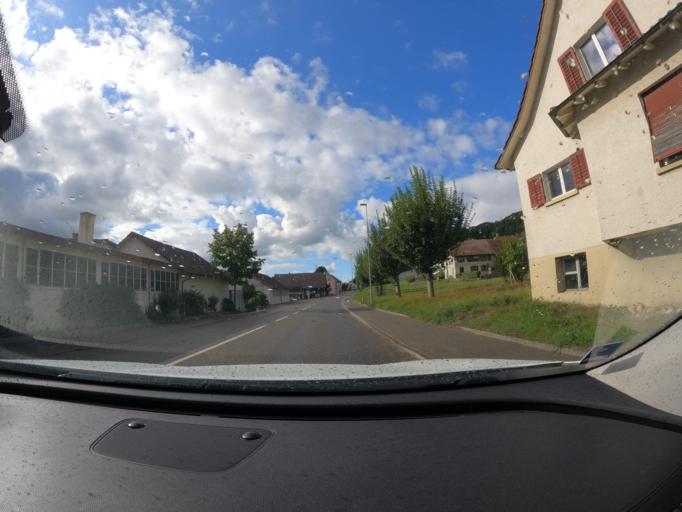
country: CH
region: Aargau
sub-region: Bezirk Kulm
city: Reinach
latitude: 47.2708
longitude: 8.1712
